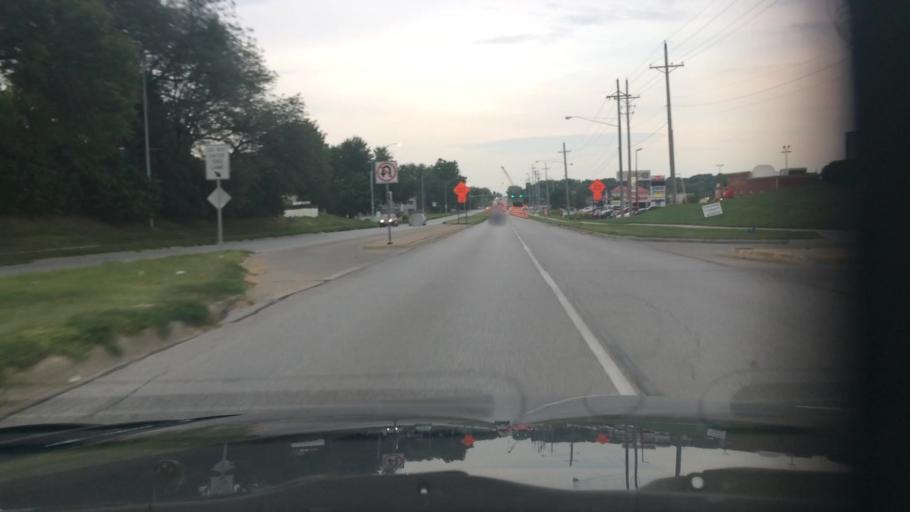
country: US
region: Nebraska
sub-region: Douglas County
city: Ralston
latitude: 41.2040
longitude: -96.0431
